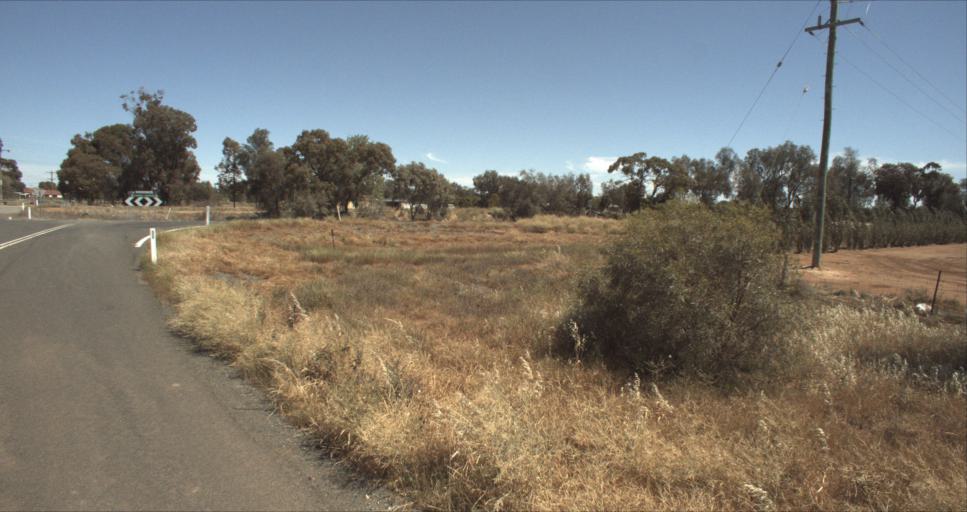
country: AU
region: New South Wales
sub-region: Leeton
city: Leeton
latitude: -34.5236
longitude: 146.3458
